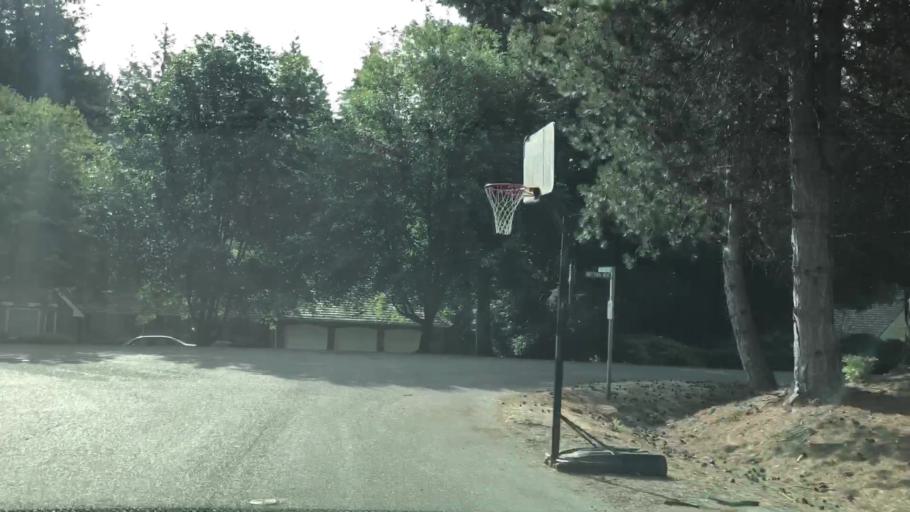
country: US
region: Washington
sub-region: King County
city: Cottage Lake
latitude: 47.7345
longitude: -122.0983
